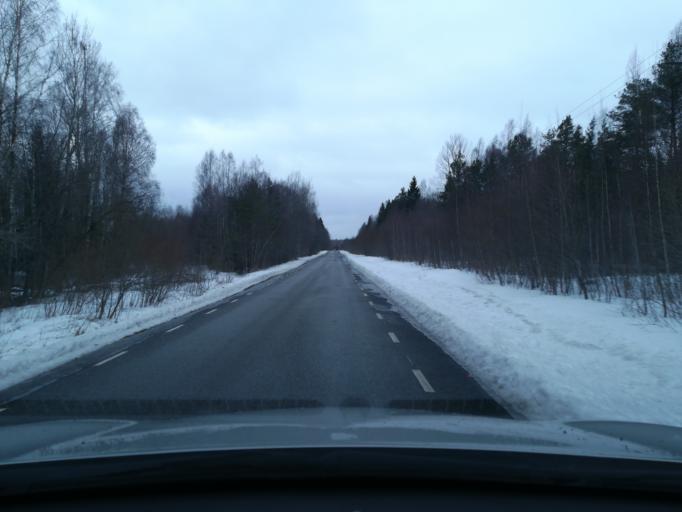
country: EE
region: Harju
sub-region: Nissi vald
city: Turba
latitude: 59.0658
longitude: 24.2528
